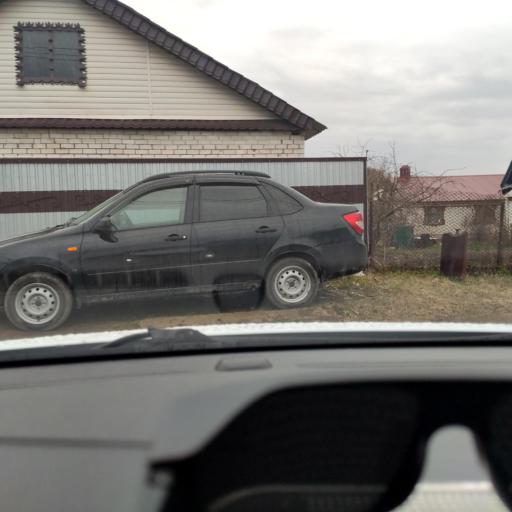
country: RU
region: Tatarstan
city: Vysokaya Gora
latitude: 55.9283
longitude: 49.3064
